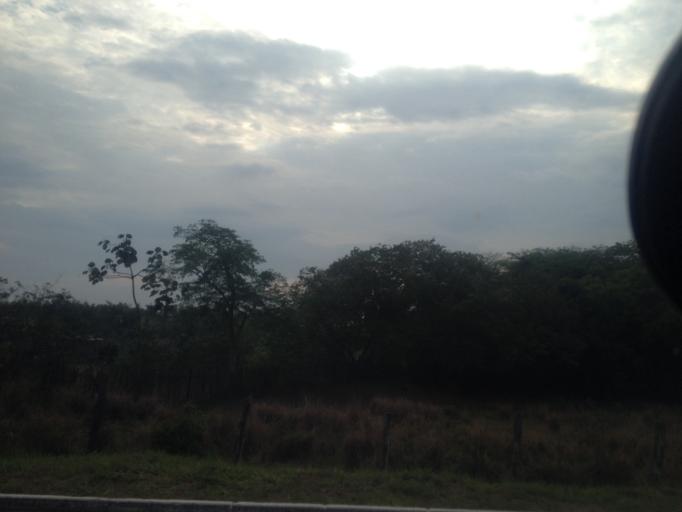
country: BR
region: Rio de Janeiro
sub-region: Porto Real
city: Porto Real
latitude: -22.4326
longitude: -44.3172
